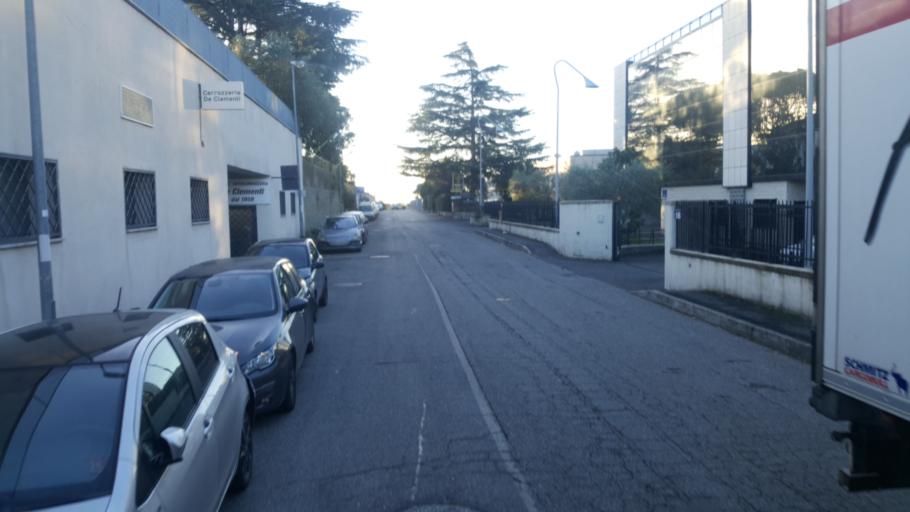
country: IT
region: Latium
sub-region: Citta metropolitana di Roma Capitale
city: Formello
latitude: 42.0526
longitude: 12.4024
